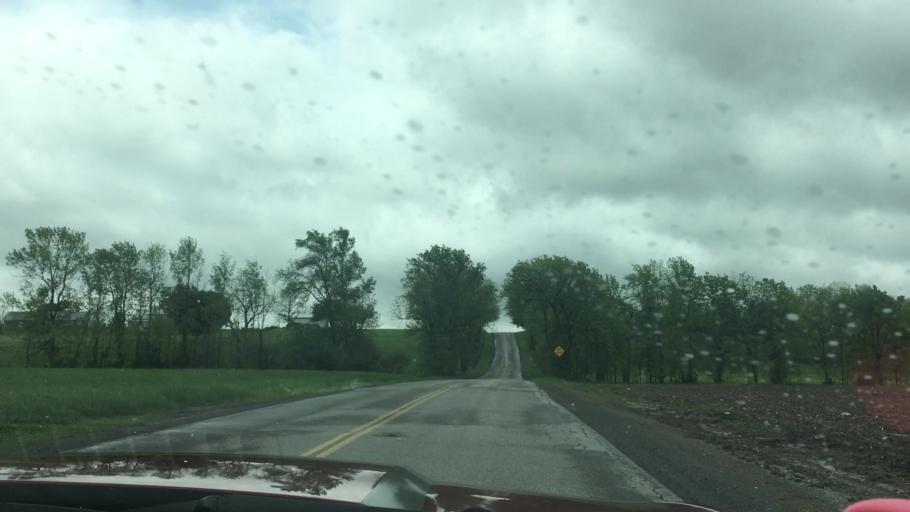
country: US
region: New York
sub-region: Genesee County
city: Batavia
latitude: 43.0869
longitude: -78.1393
